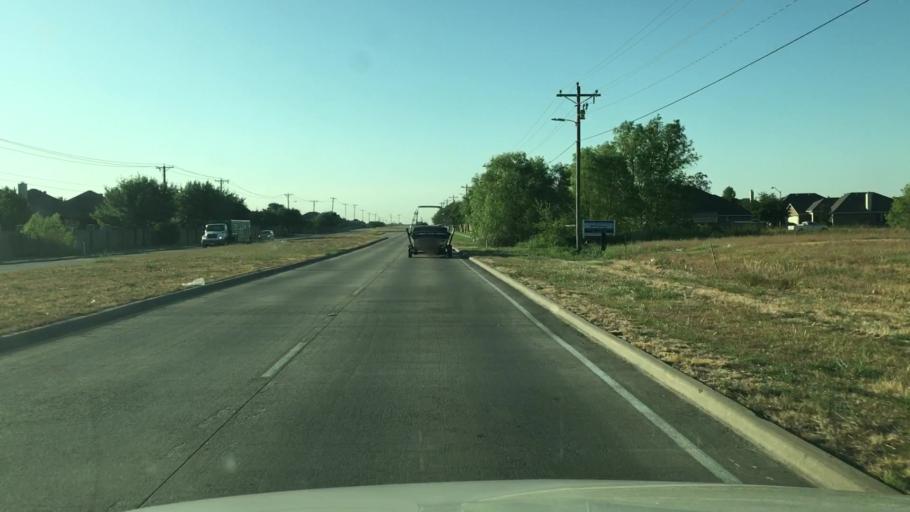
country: US
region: Texas
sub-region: Johnson County
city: Burleson
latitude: 32.5368
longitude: -97.3584
